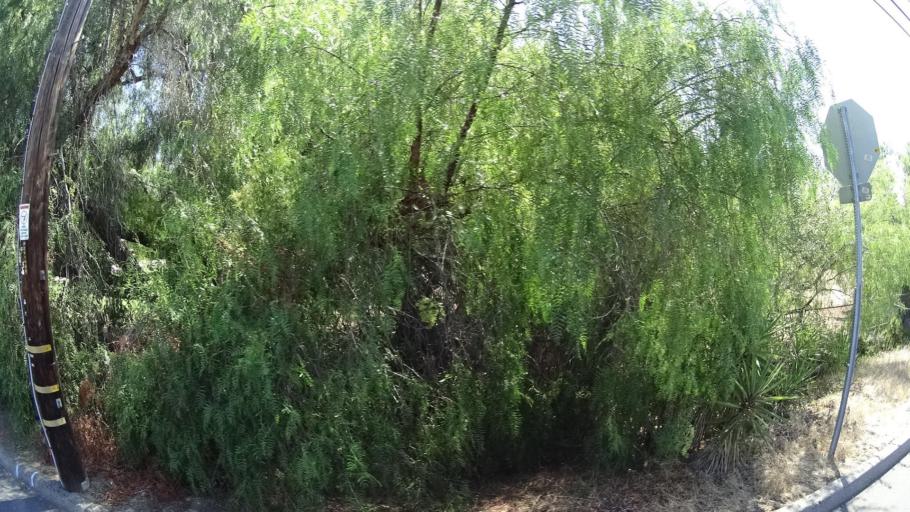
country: US
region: California
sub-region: San Diego County
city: Escondido
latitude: 33.0847
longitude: -117.0908
